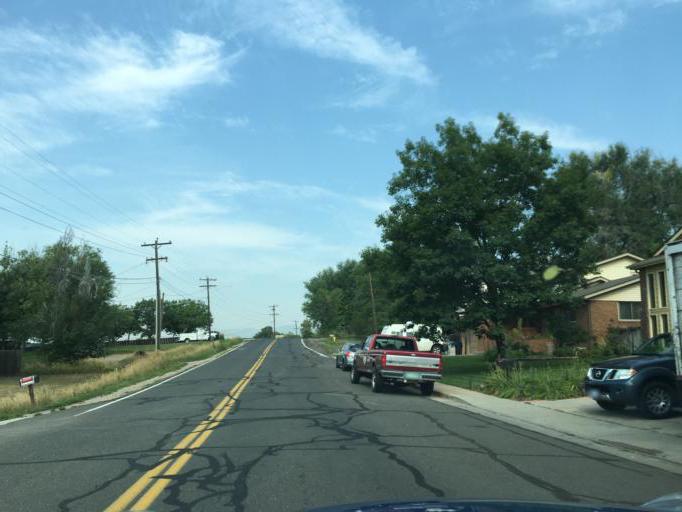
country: US
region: Colorado
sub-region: Jefferson County
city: Arvada
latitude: 39.8093
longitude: -105.0826
